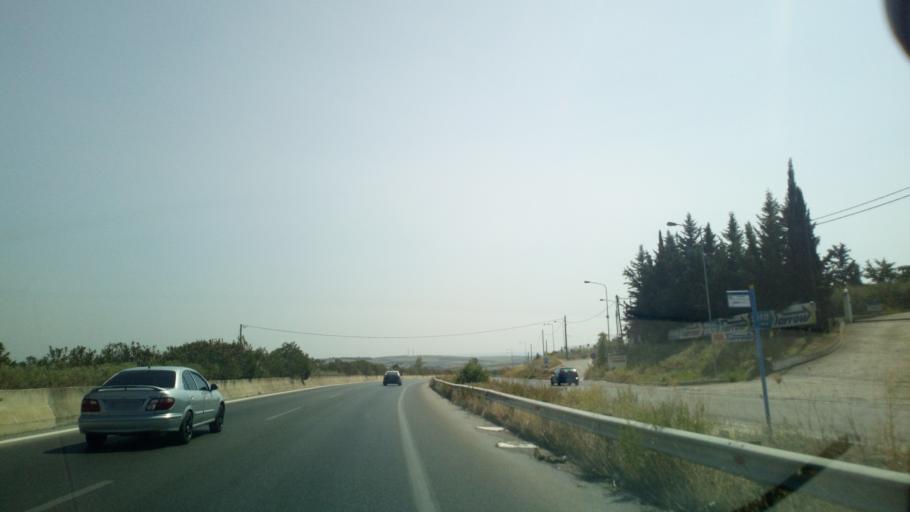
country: GR
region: Central Macedonia
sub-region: Nomos Thessalonikis
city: Kato Scholari
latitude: 40.4205
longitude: 23.0229
